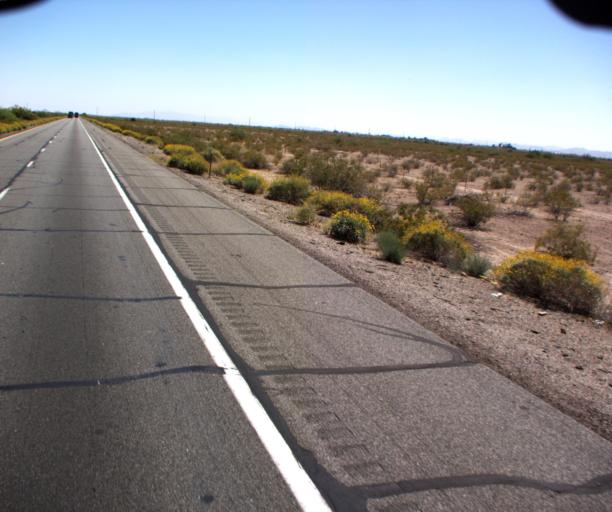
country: US
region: Arizona
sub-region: Maricopa County
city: Buckeye
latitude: 33.4763
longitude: -112.8432
